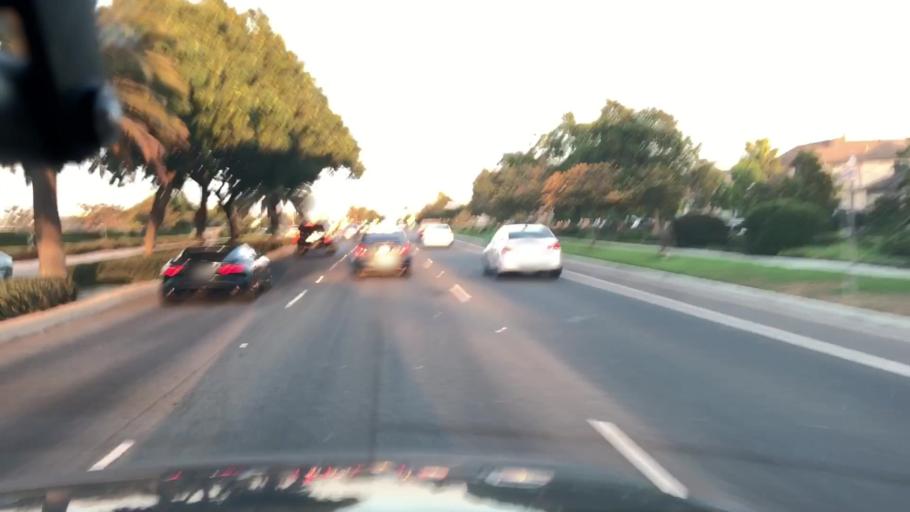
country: US
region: California
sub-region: Ventura County
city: El Rio
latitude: 34.2189
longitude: -119.1645
